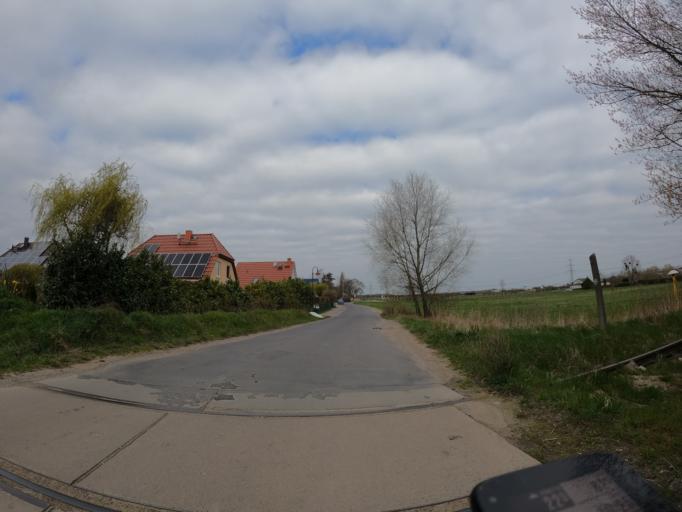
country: DE
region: Brandenburg
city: Neuenhagen
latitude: 52.5344
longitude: 13.6981
